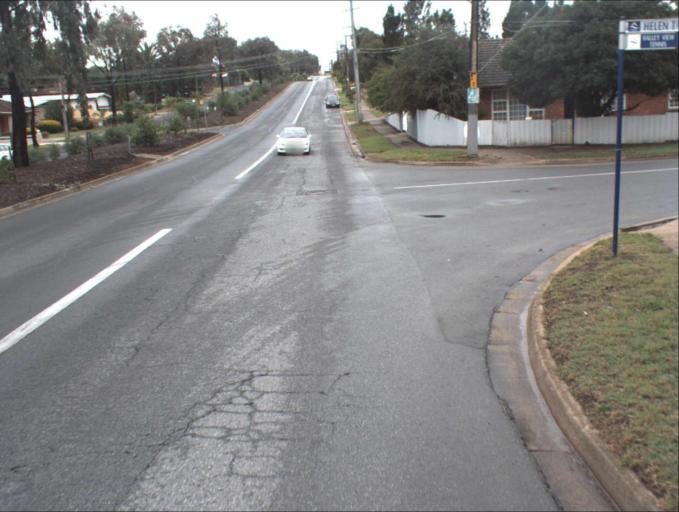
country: AU
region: South Australia
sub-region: Port Adelaide Enfield
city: Gilles Plains
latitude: -34.8395
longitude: 138.6627
